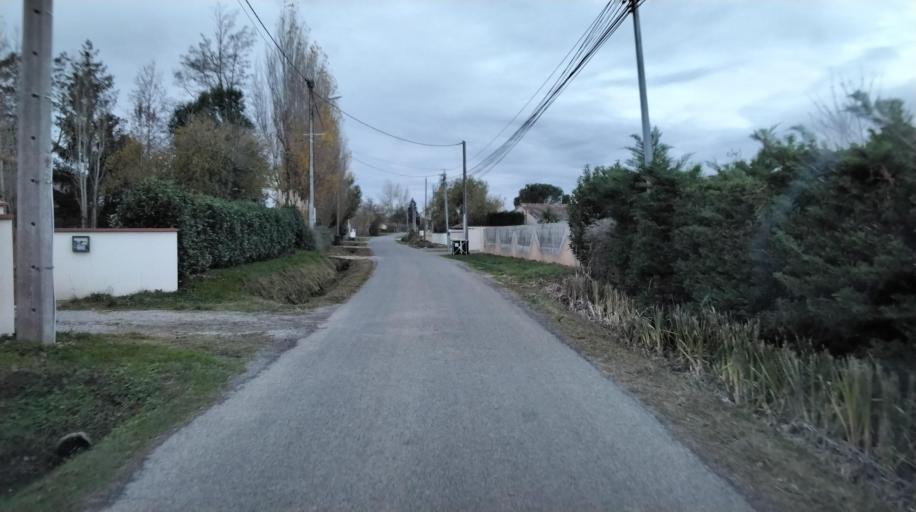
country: FR
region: Midi-Pyrenees
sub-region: Departement de la Haute-Garonne
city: Berat
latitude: 43.3900
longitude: 1.1952
